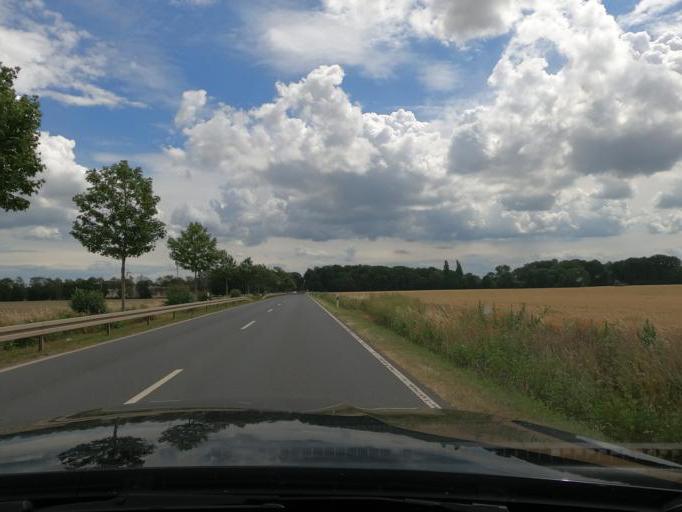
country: DE
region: Lower Saxony
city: Sehnde
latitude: 52.3364
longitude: 9.9360
